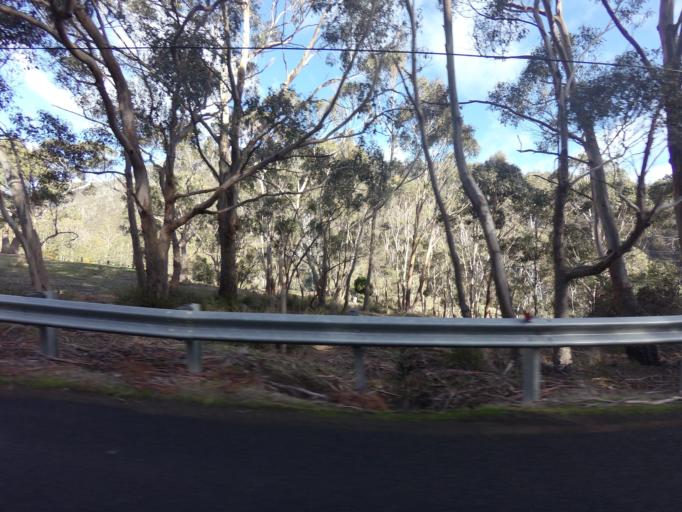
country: AU
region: Tasmania
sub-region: Glenorchy
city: Berriedale
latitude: -42.8119
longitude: 147.1728
